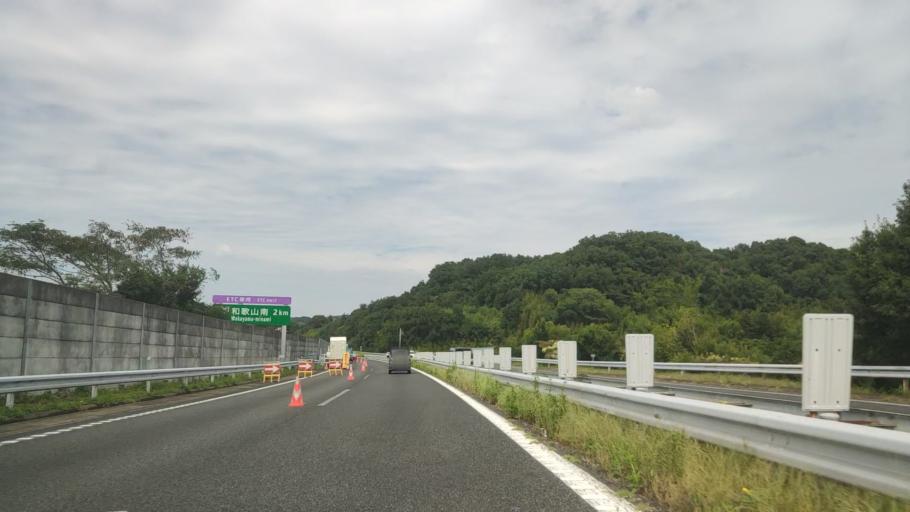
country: JP
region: Wakayama
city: Kainan
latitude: 34.1901
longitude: 135.2385
